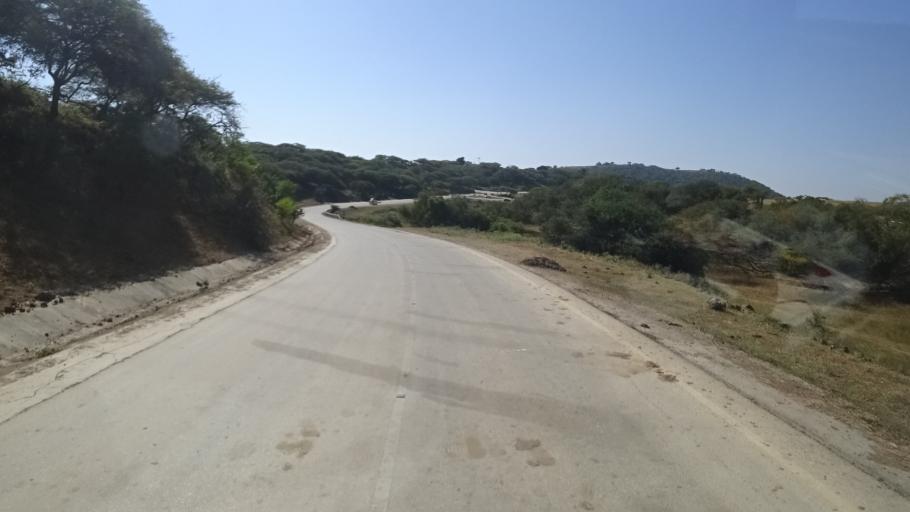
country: OM
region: Zufar
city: Salalah
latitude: 17.0661
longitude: 54.6007
